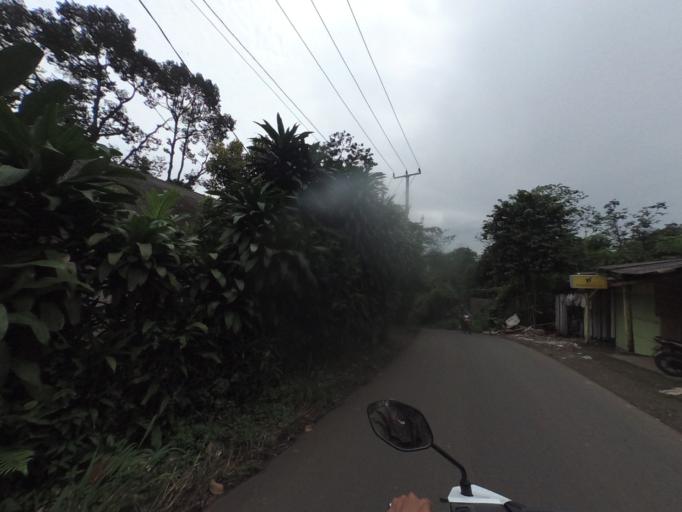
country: ID
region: West Java
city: Bogor
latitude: -6.6372
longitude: 106.7445
